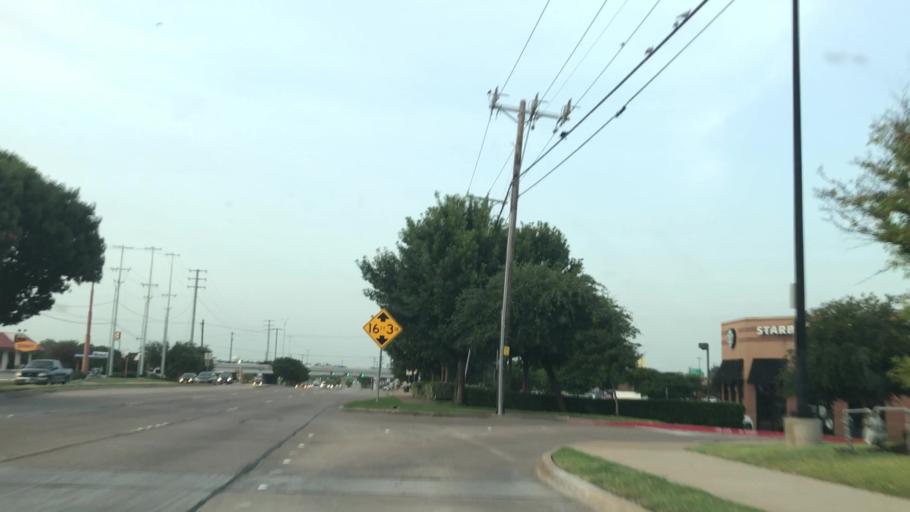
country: US
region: Texas
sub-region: Dallas County
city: Sunnyvale
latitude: 32.8428
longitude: -96.5957
